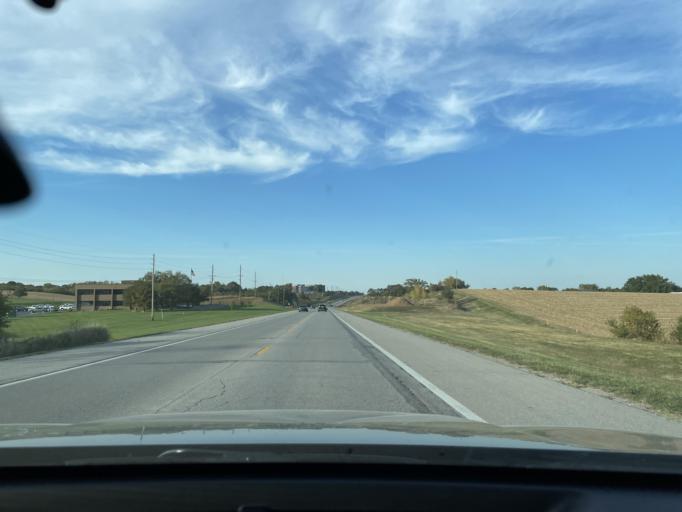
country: US
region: Missouri
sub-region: Buchanan County
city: Saint Joseph
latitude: 39.7604
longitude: -94.7685
